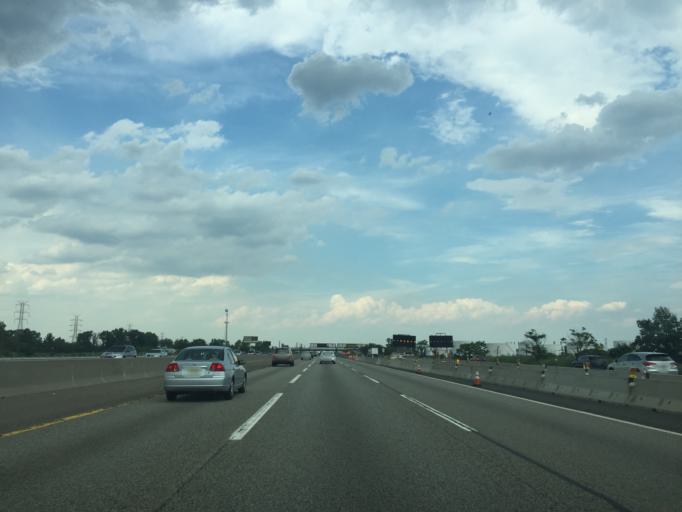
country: US
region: New Jersey
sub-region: Union County
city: Linden
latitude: 40.6049
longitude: -74.2280
